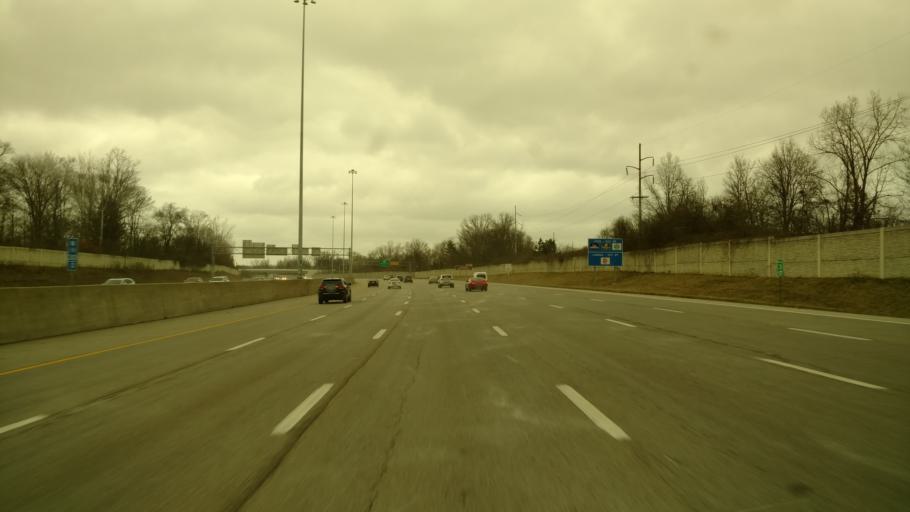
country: US
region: Ohio
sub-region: Franklin County
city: Huber Ridge
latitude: 40.0897
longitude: -82.9070
